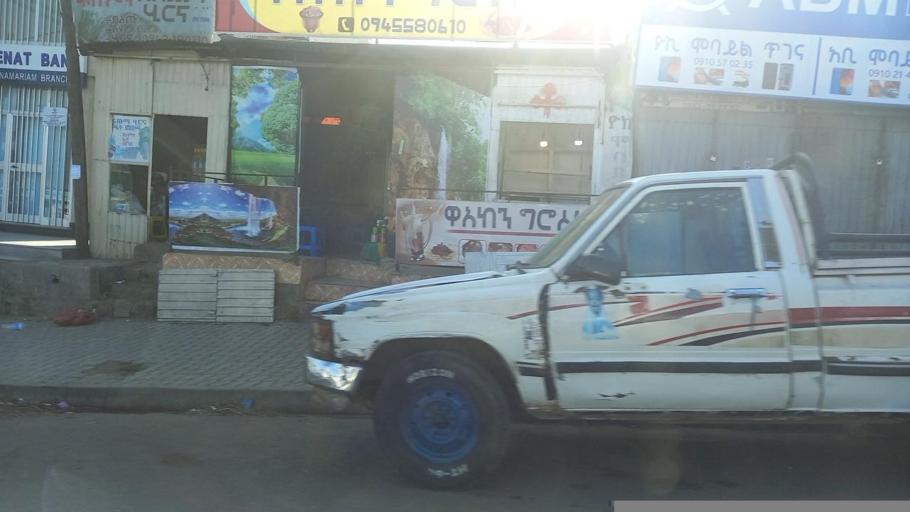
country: ET
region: Adis Abeba
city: Addis Ababa
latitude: 8.9342
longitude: 38.7439
